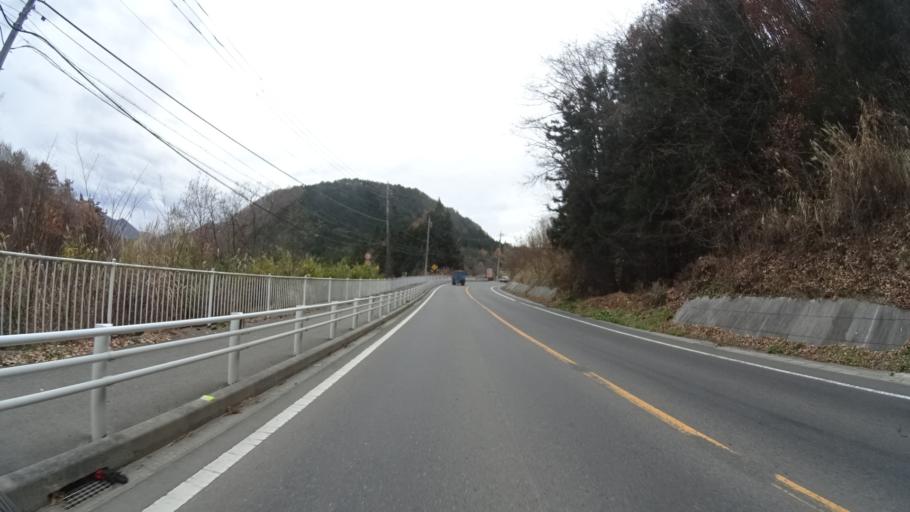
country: JP
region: Gunma
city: Numata
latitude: 36.6694
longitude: 139.1893
